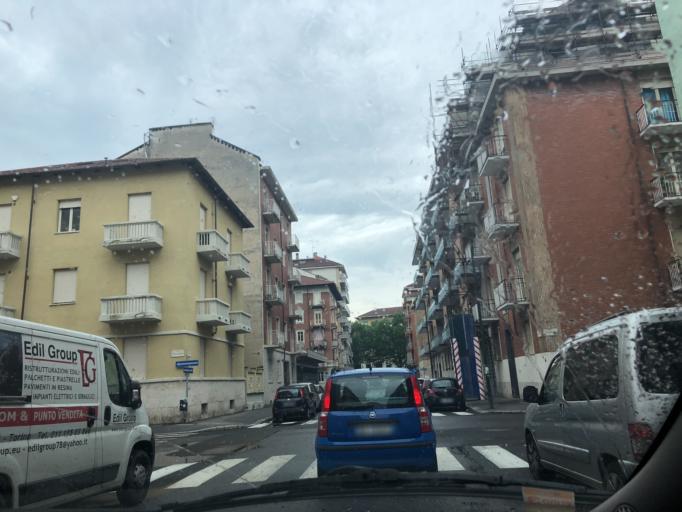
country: IT
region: Piedmont
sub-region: Provincia di Torino
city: Lesna
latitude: 45.0787
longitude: 7.6349
